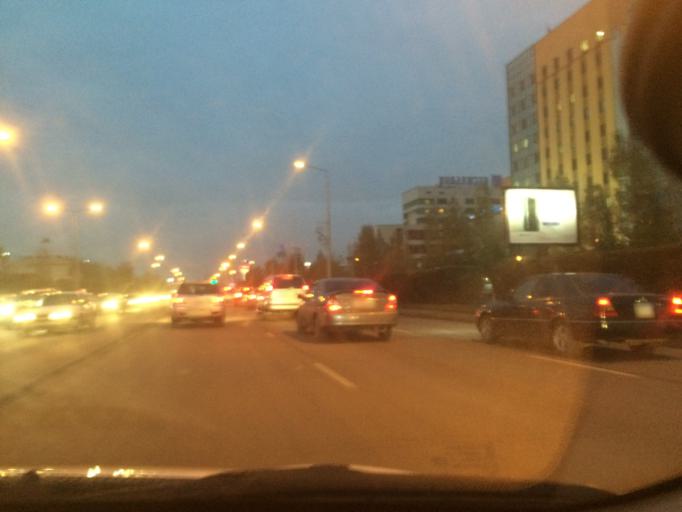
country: KZ
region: Astana Qalasy
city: Astana
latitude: 51.1414
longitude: 71.4104
